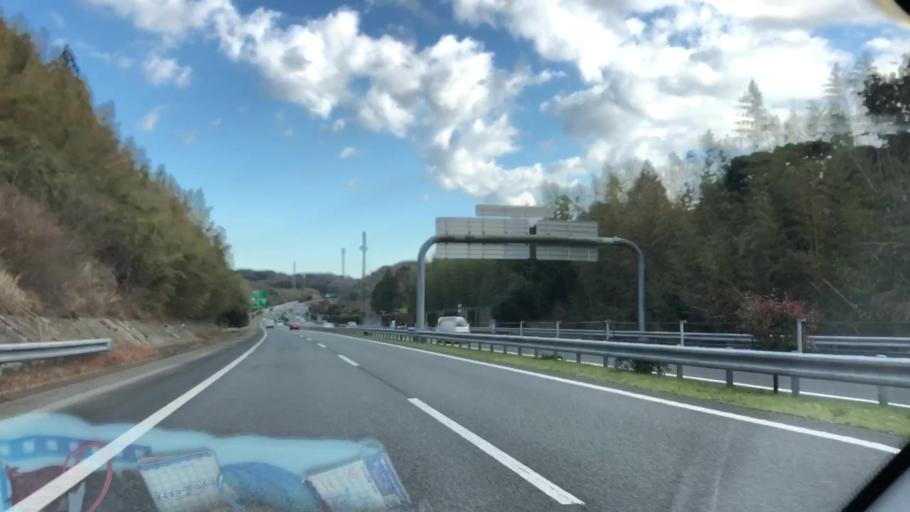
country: JP
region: Chiba
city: Kisarazu
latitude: 35.3592
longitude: 139.9548
